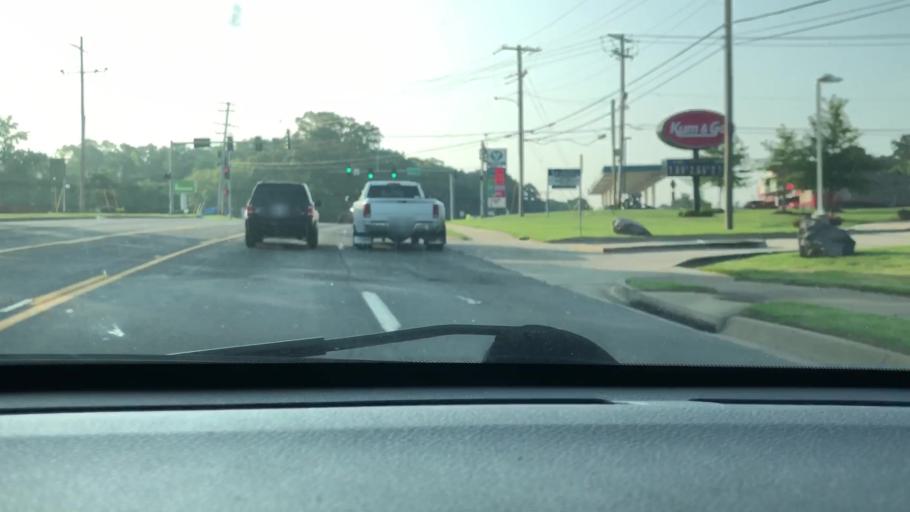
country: US
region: Arkansas
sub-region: Saline County
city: Bryant
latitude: 34.6104
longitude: -92.4941
